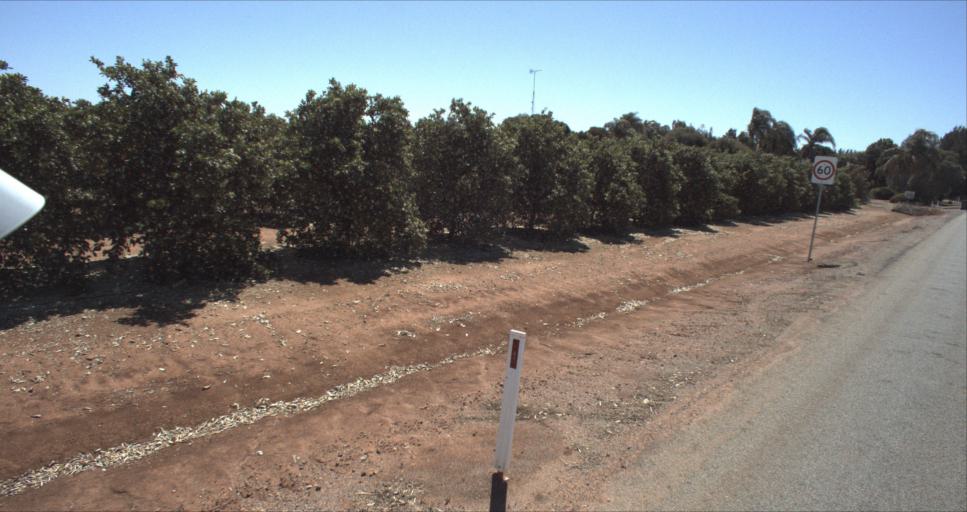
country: AU
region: New South Wales
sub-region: Leeton
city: Leeton
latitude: -34.5317
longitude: 146.3289
